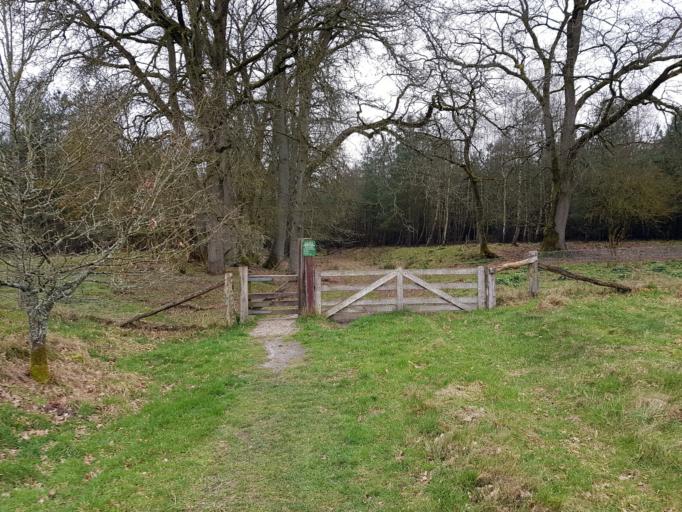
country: NL
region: Gelderland
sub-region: Gemeente Epe
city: Vaassen
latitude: 52.2845
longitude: 5.8997
